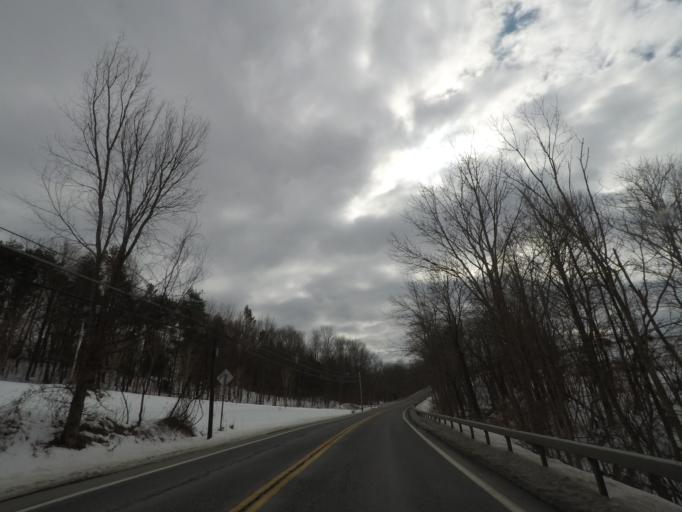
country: US
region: New York
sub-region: Washington County
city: Greenwich
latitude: 43.0806
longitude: -73.4831
